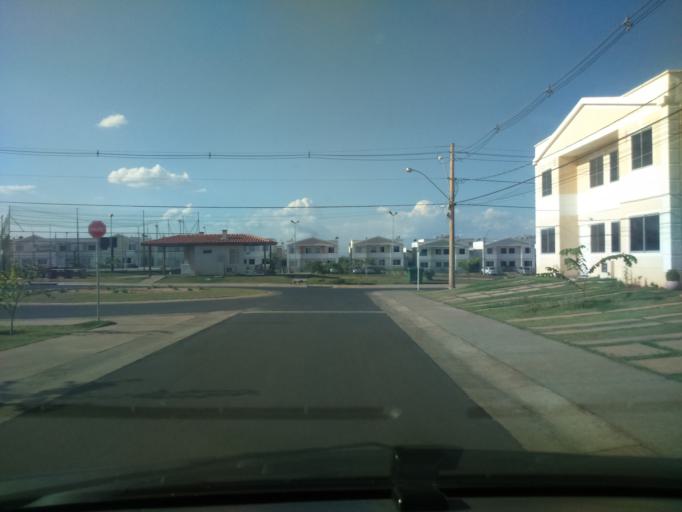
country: BR
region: Federal District
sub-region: Brasilia
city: Brasilia
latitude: -15.8889
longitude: -47.8121
